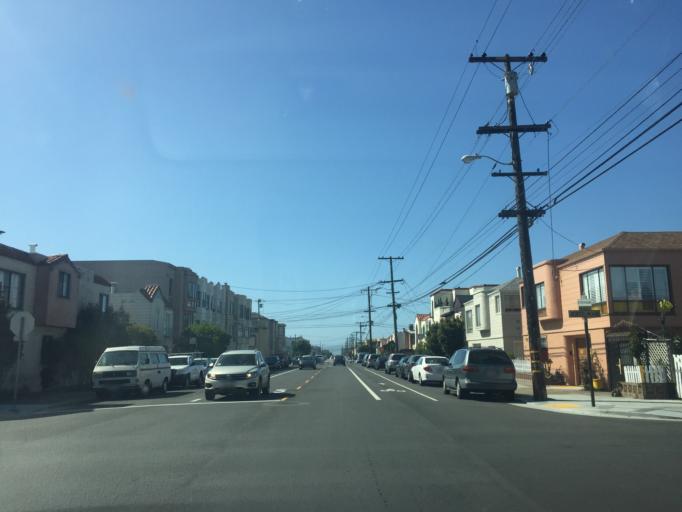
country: US
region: California
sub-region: San Mateo County
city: Daly City
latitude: 37.7597
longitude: -122.4811
